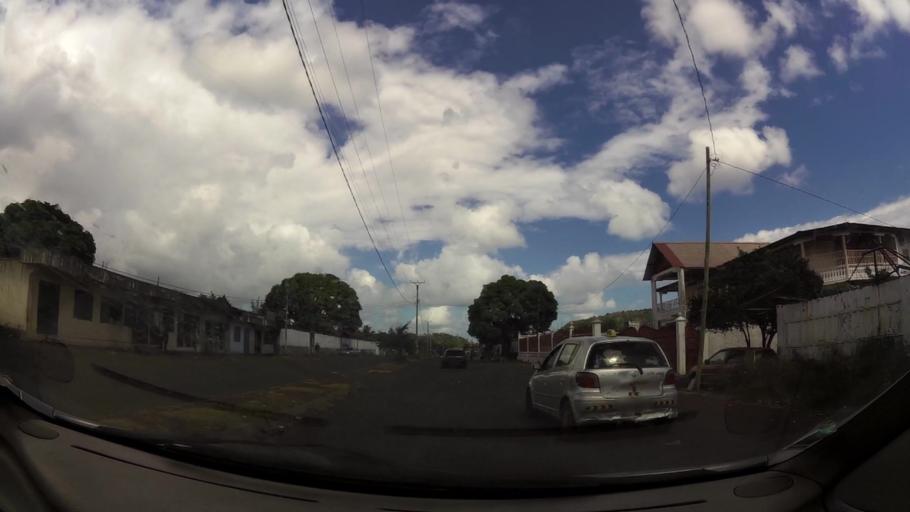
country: KM
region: Grande Comore
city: Mavingouni
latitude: -11.7245
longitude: 43.2449
